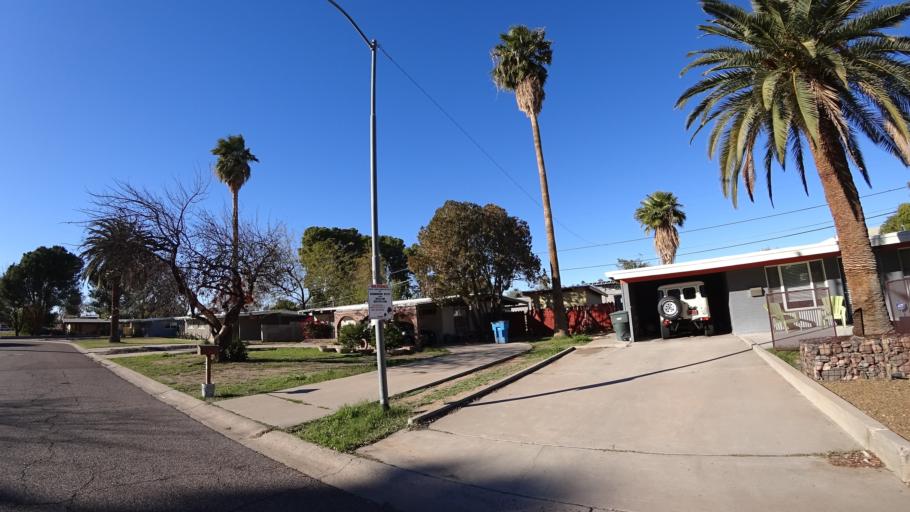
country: US
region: Arizona
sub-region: Maricopa County
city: Phoenix
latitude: 33.5216
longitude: -112.0491
